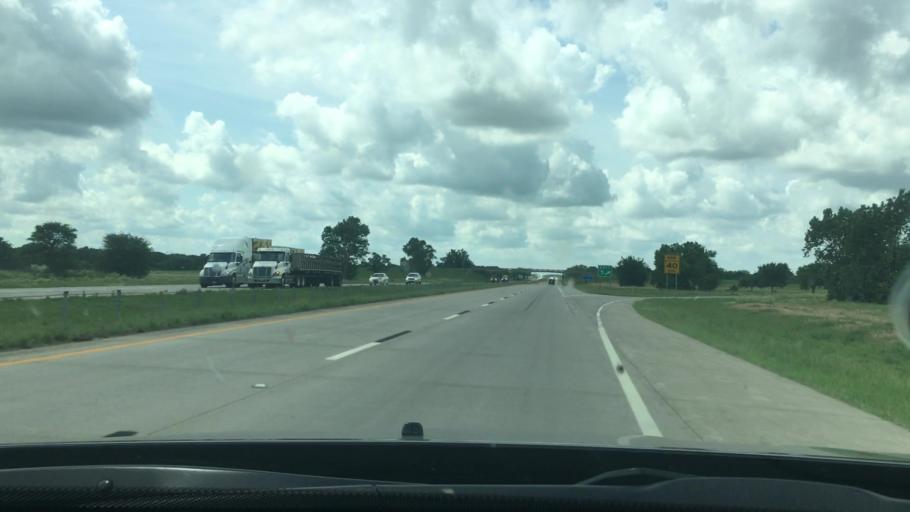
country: US
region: Oklahoma
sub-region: Love County
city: Marietta
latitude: 33.7993
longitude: -97.1350
